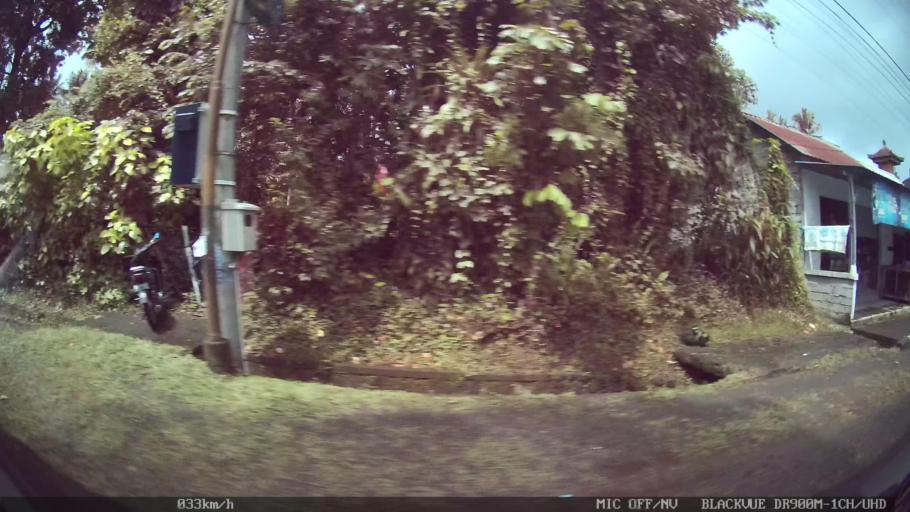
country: ID
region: Bali
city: Pegongan
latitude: -8.4872
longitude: 115.2264
